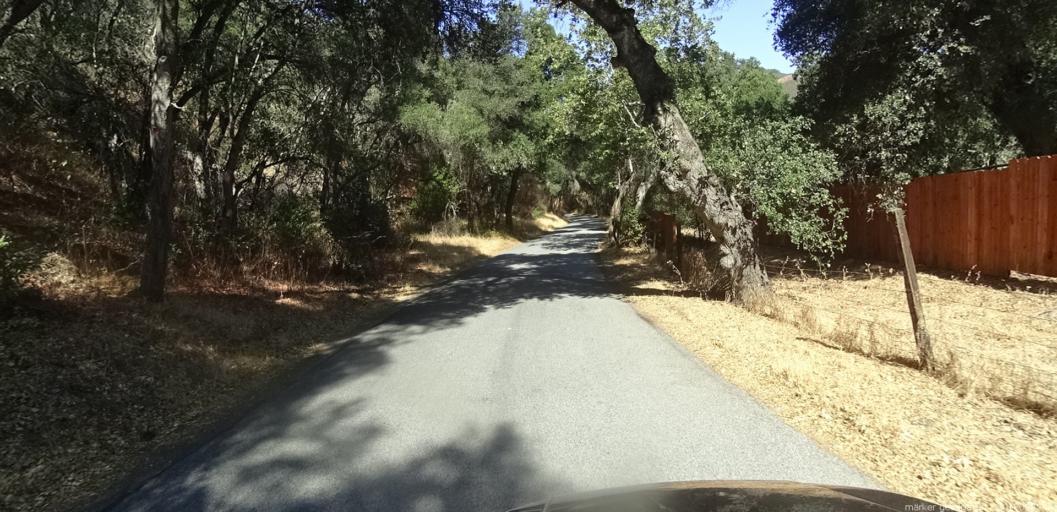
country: US
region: California
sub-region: Monterey County
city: Carmel Valley Village
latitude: 36.3924
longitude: -121.6070
